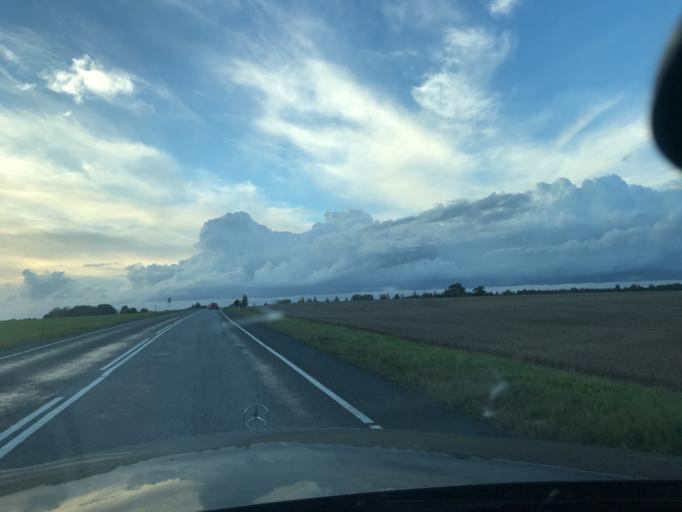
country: EE
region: Vorumaa
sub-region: Antsla vald
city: Vana-Antsla
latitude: 57.8816
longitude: 26.5388
